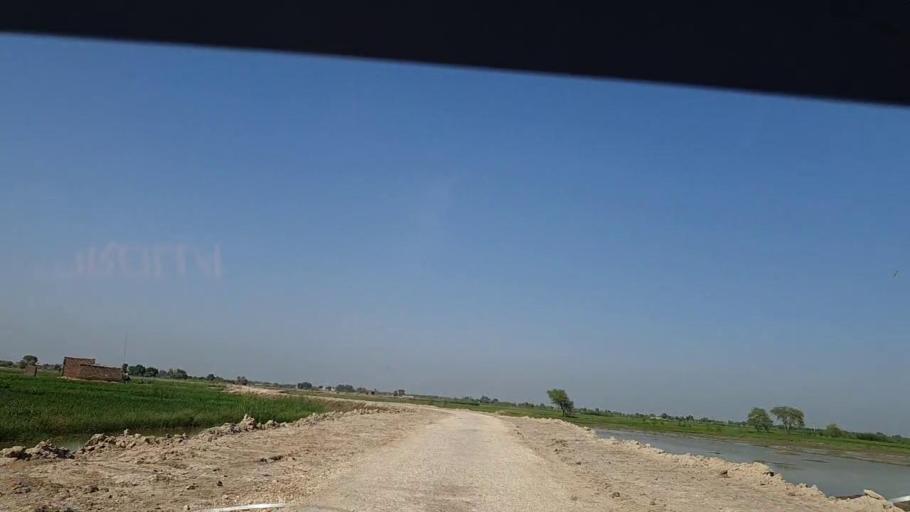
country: PK
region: Sindh
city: Tangwani
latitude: 28.3184
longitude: 69.0830
